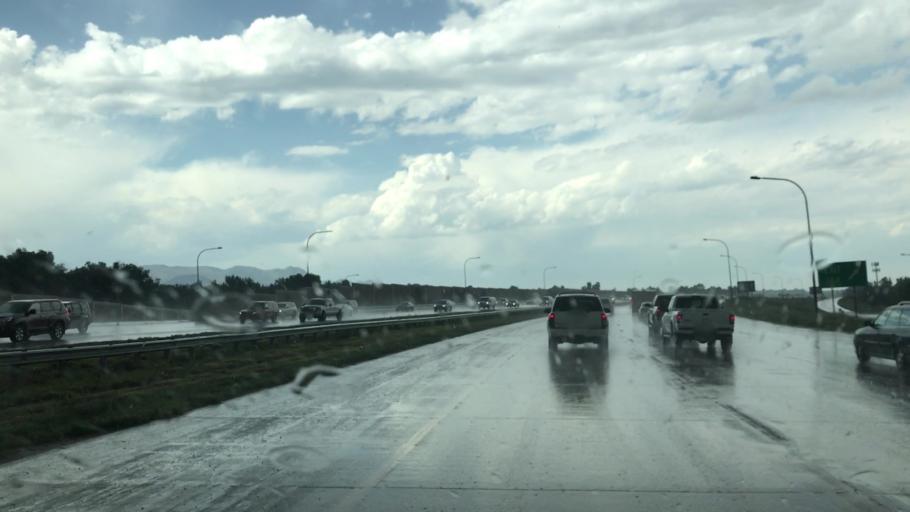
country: US
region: Colorado
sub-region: El Paso County
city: Colorado Springs
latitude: 38.8576
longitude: -104.8339
